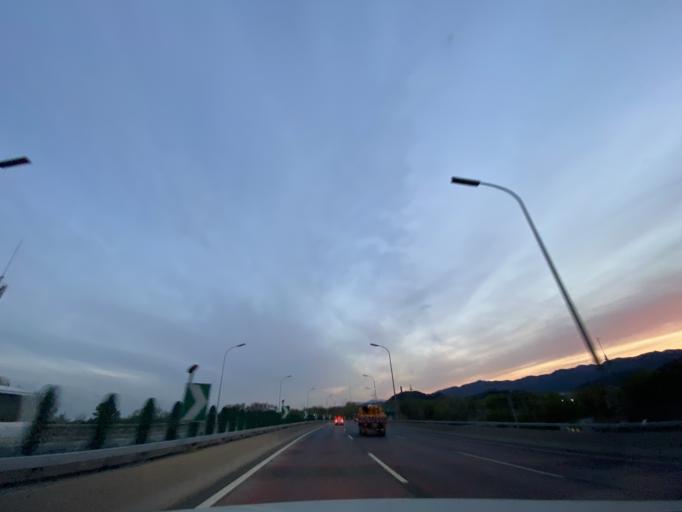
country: CN
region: Beijing
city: Haidian
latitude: 40.0044
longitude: 116.2635
